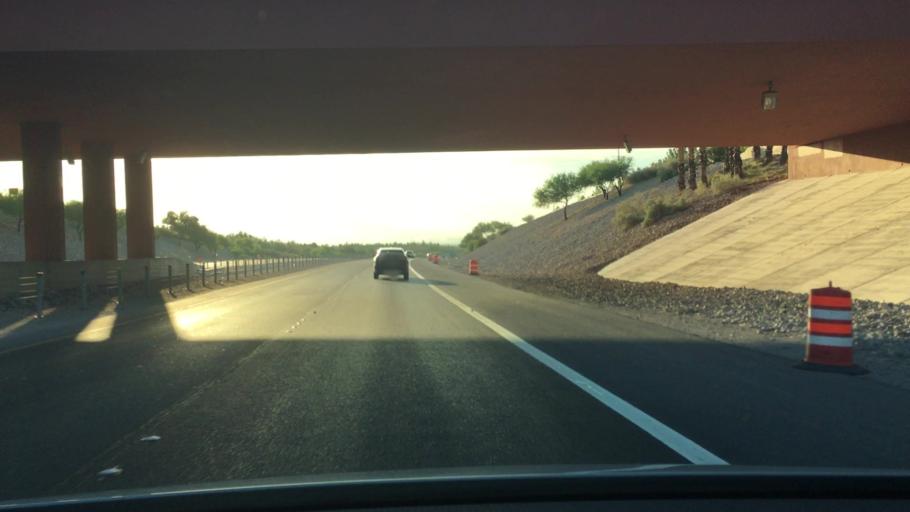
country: US
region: Nevada
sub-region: Clark County
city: Summerlin South
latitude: 36.1935
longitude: -115.3238
